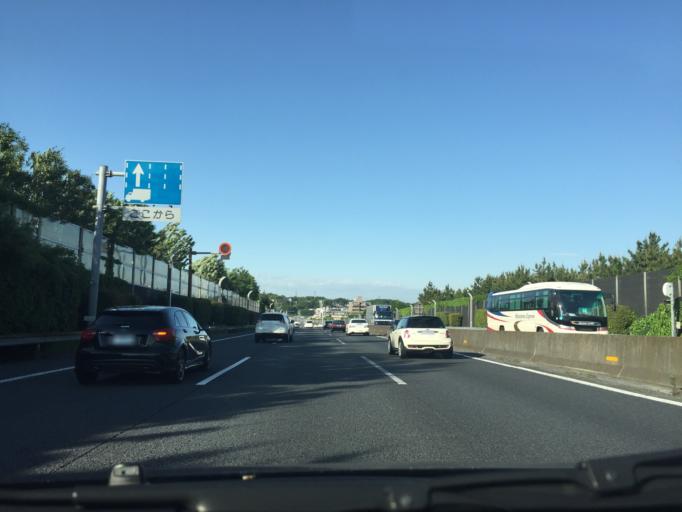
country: JP
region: Tokyo
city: Chofugaoka
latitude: 35.5961
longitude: 139.5755
